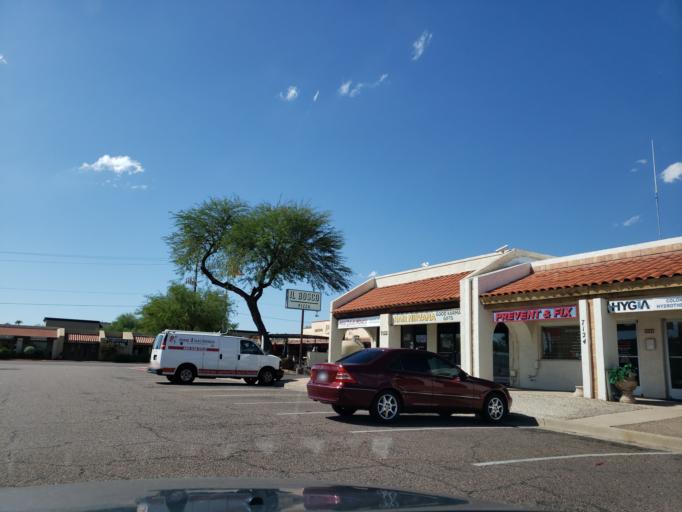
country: US
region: Arizona
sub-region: Maricopa County
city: Paradise Valley
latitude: 33.5829
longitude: -111.9270
